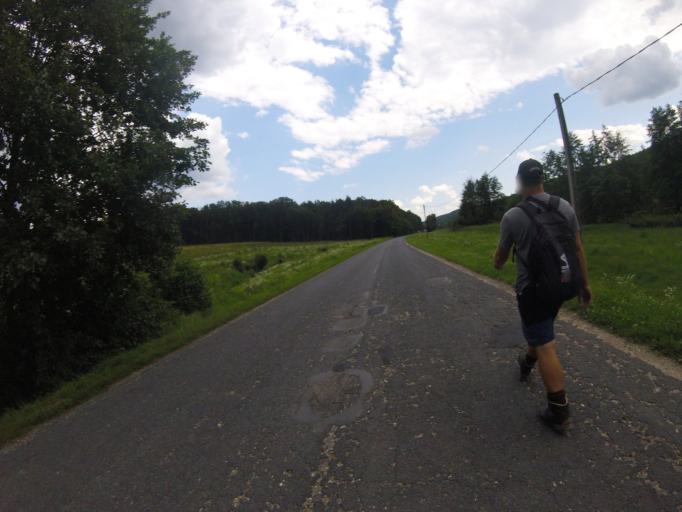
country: HU
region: Zala
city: Becsehely
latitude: 46.5003
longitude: 16.7391
